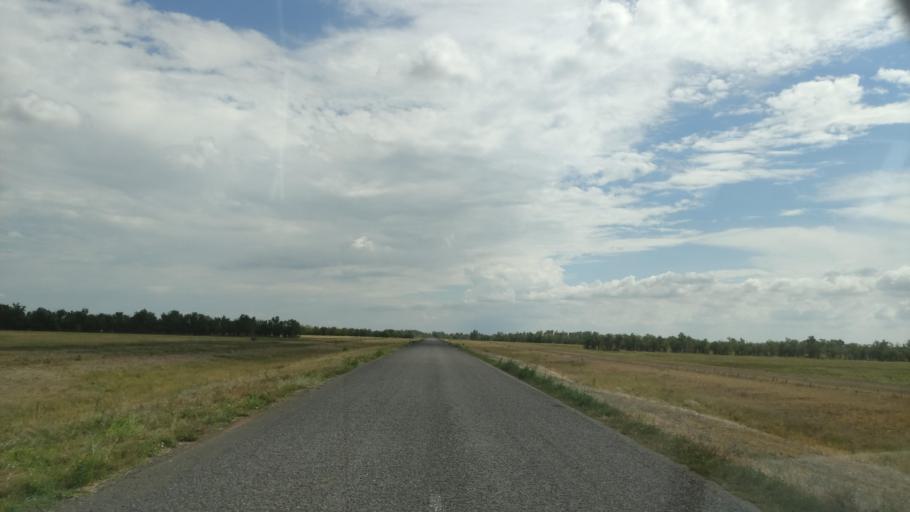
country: KZ
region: Pavlodar
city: Pavlodar
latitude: 52.6367
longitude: 76.9771
